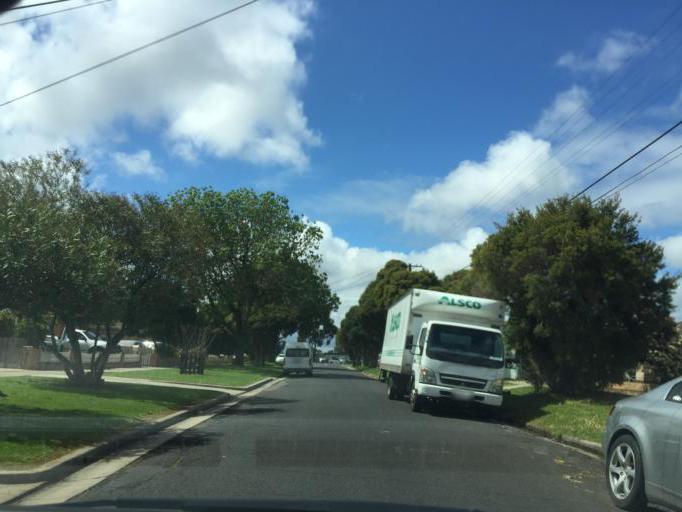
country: AU
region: Victoria
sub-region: Maribyrnong
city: Braybrook
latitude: -37.7771
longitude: 144.8457
